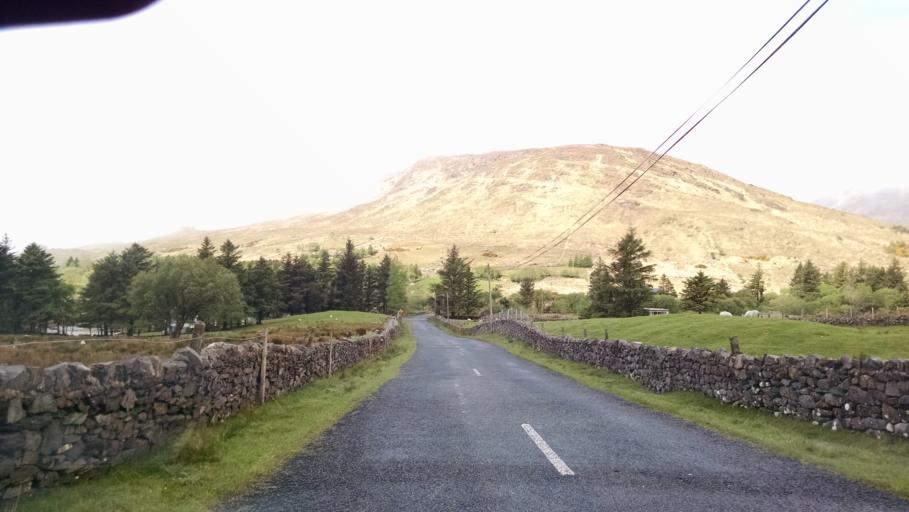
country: IE
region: Connaught
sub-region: County Galway
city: Clifden
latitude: 53.6069
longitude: -9.7480
